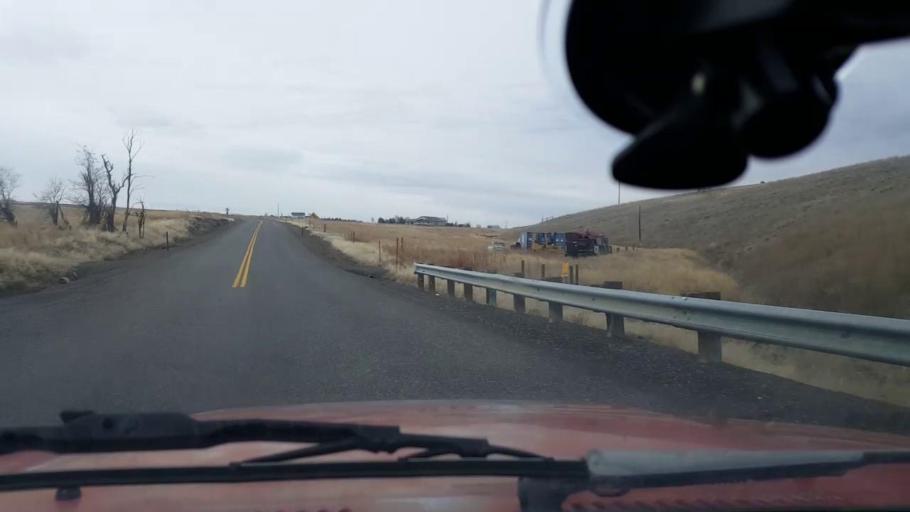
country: US
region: Washington
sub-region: Asotin County
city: Clarkston Heights-Vineland
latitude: 46.3784
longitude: -117.1482
